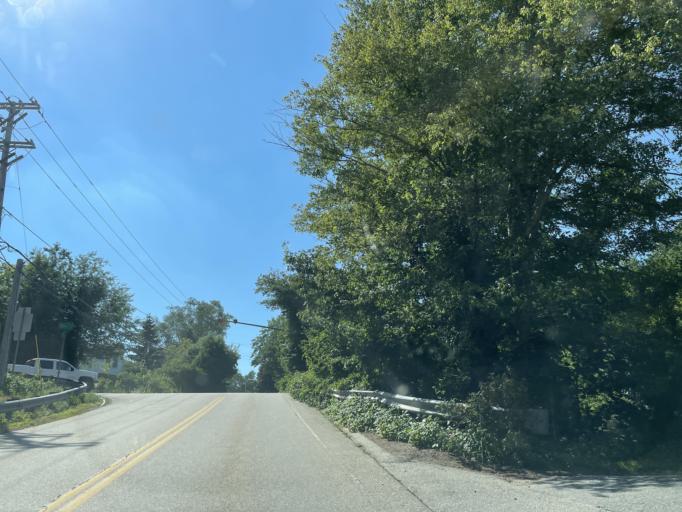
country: US
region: Massachusetts
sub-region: Worcester County
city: East Douglas
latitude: 42.0747
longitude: -71.7049
